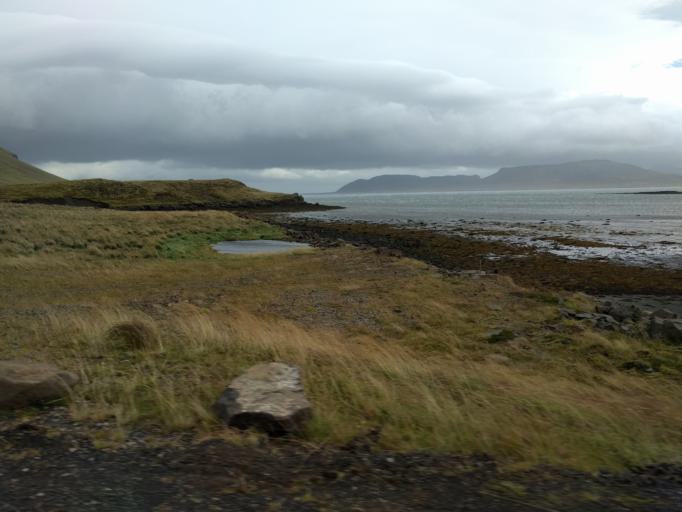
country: IS
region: West
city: Olafsvik
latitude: 64.9238
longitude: -23.2980
